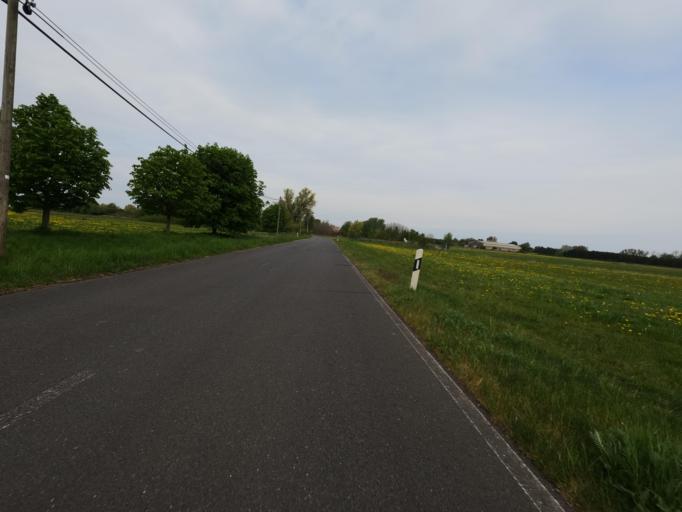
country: DE
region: Mecklenburg-Vorpommern
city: Born
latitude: 54.3569
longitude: 12.5662
